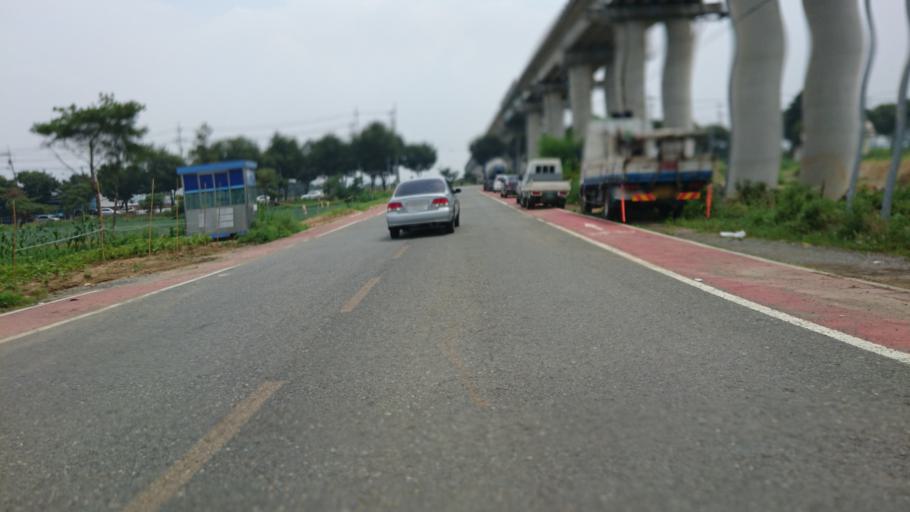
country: KR
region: Gyeongsangbuk-do
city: Gyeongsan-si
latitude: 35.8556
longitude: 128.7200
